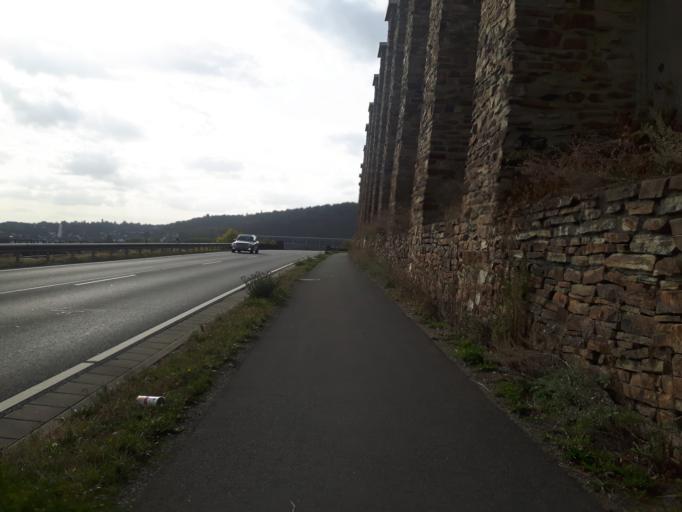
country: DE
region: Rheinland-Pfalz
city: Andernach
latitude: 50.4450
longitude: 7.4102
